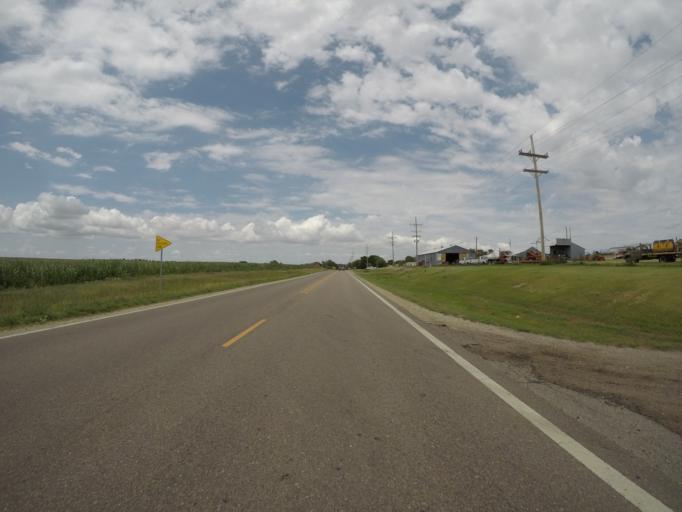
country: US
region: Kansas
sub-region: Rawlins County
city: Atwood
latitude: 39.7961
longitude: -101.0468
